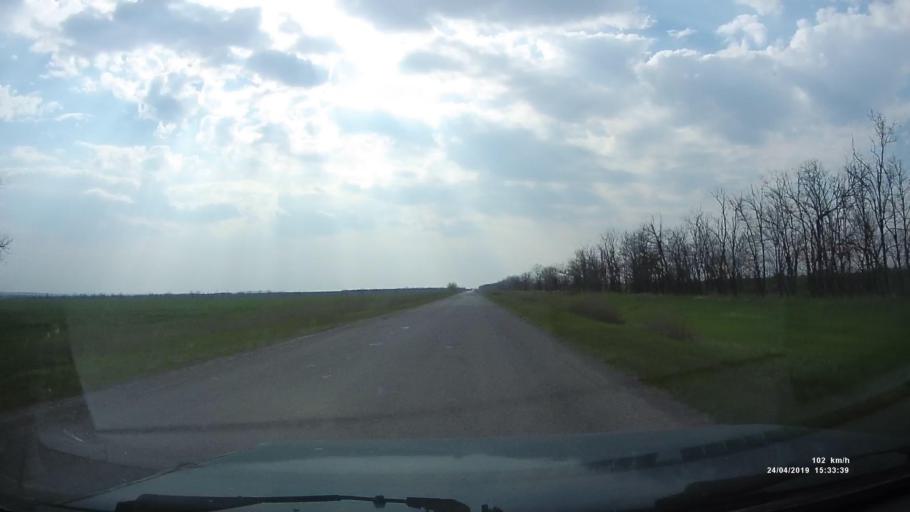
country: RU
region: Kalmykiya
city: Yashalta
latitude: 46.5991
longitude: 42.9346
